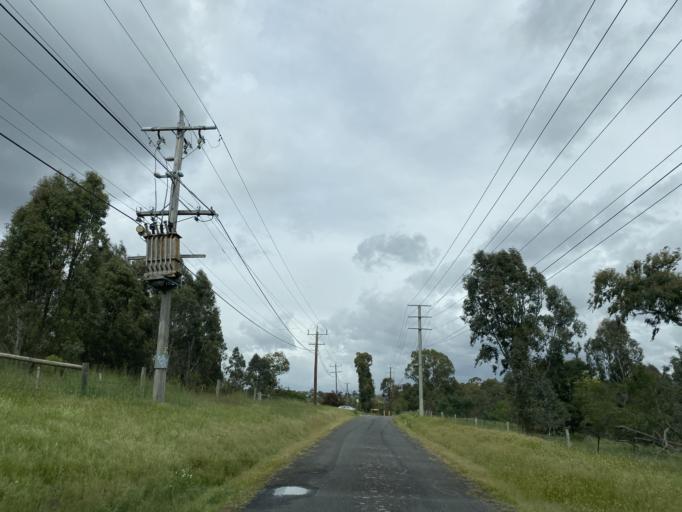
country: AU
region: Victoria
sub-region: Banyule
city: Darch
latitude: -37.7523
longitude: 145.1129
